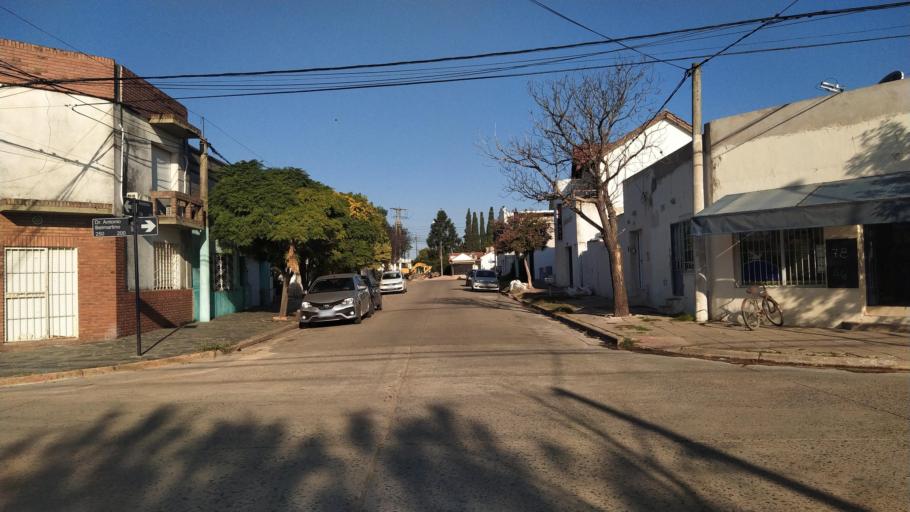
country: AR
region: Buenos Aires
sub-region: Partido de Salto
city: Salto
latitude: -34.2885
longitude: -60.2578
